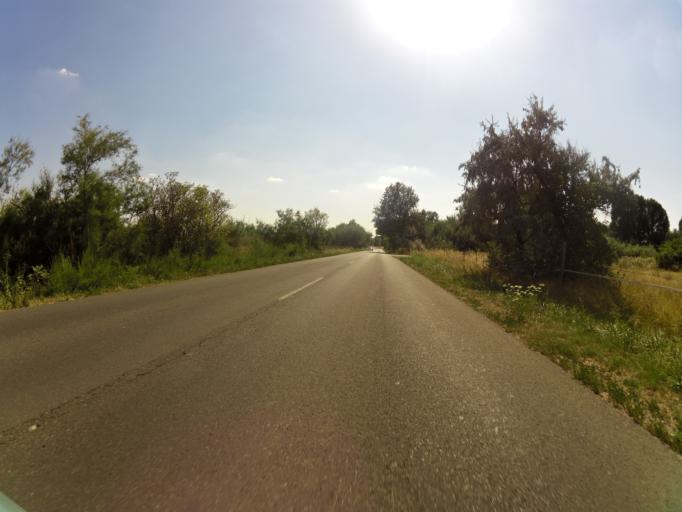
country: HU
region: Csongrad
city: Szatymaz
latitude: 46.3510
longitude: 20.0636
